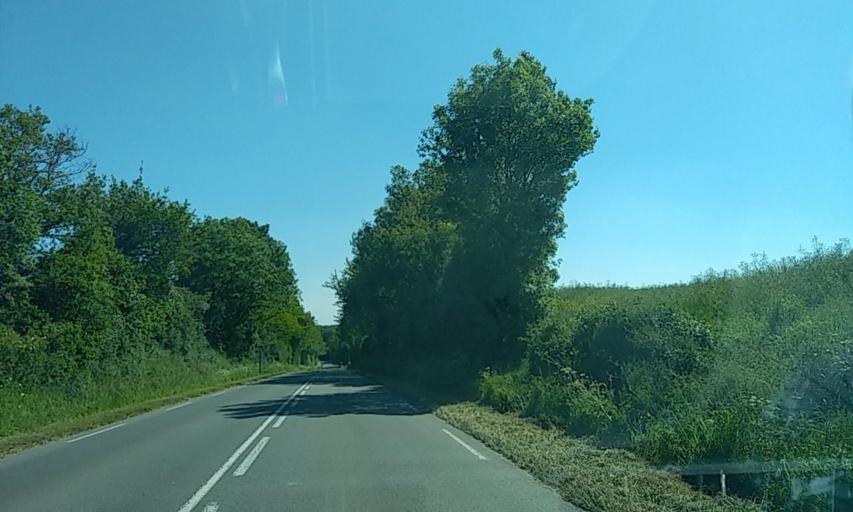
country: FR
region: Poitou-Charentes
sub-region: Departement des Deux-Sevres
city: La Chapelle-Saint-Laurent
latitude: 46.7800
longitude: -0.4779
